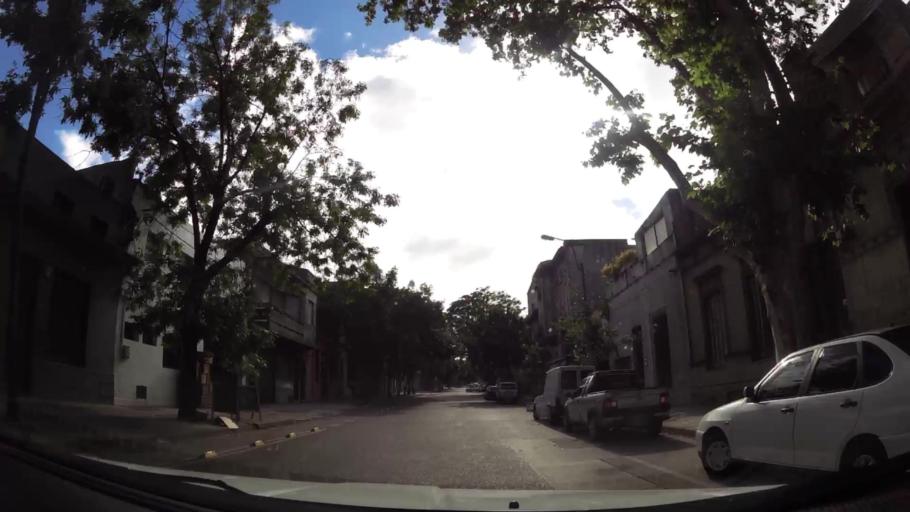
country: UY
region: Montevideo
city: Montevideo
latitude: -34.8896
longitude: -56.1754
